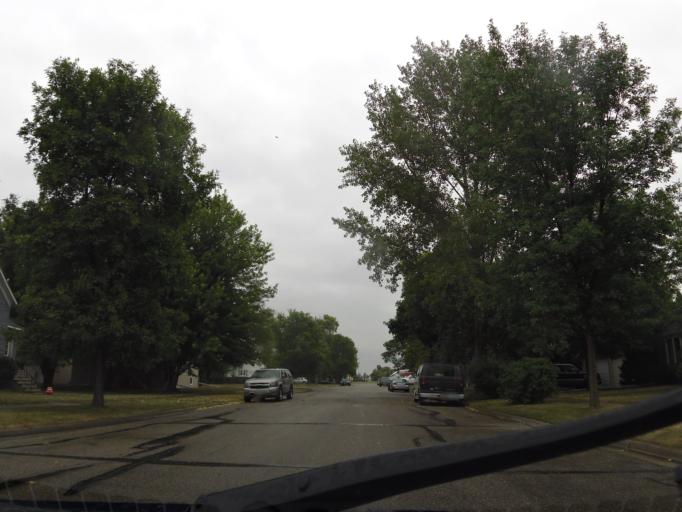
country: US
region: Minnesota
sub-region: Marshall County
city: Warren
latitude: 48.4518
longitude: -96.8779
